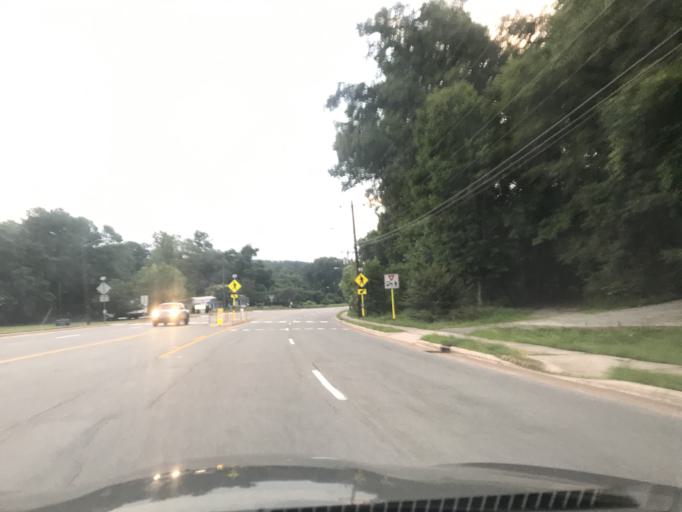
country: US
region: North Carolina
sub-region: Orange County
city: Chapel Hill
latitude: 35.9237
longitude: -79.0384
